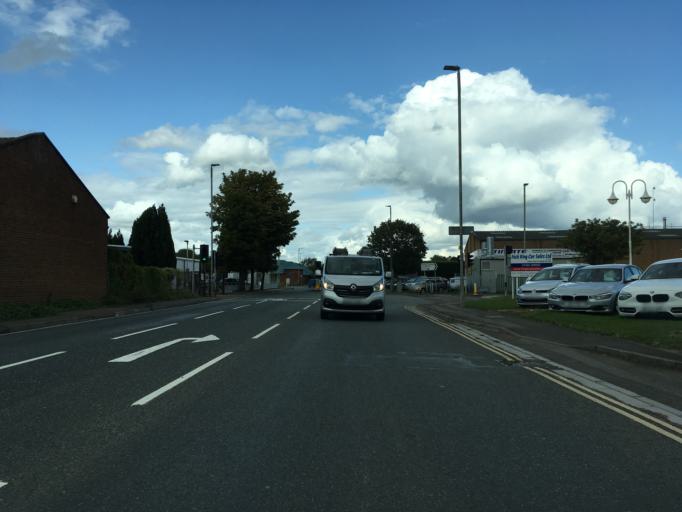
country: GB
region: England
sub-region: Gloucestershire
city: Gloucester
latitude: 51.8447
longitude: -2.2643
